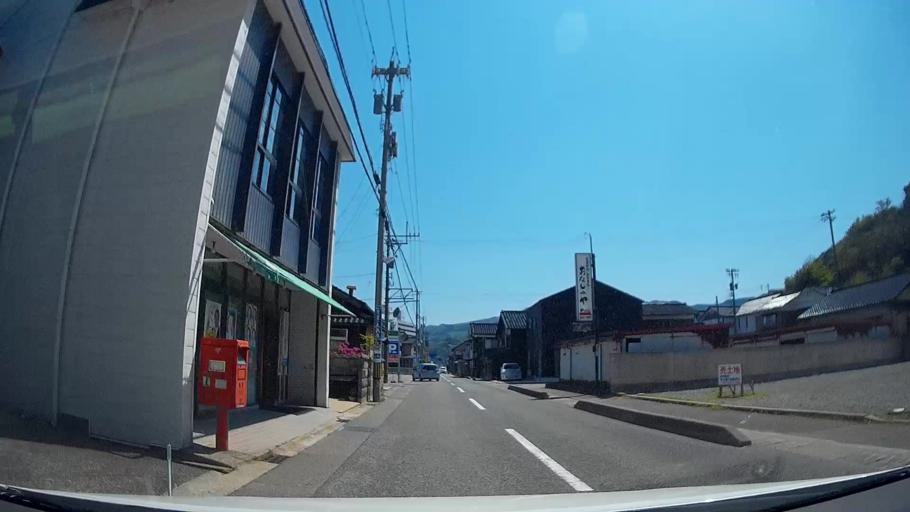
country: JP
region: Ishikawa
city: Nanao
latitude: 37.3939
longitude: 136.9115
